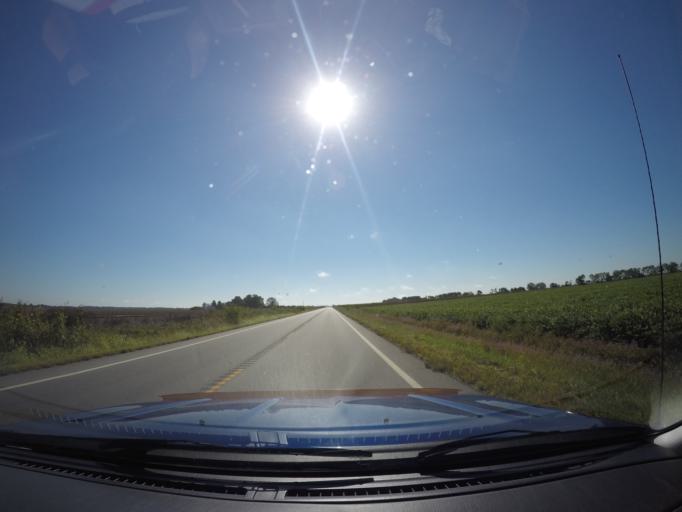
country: US
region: Kansas
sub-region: Shawnee County
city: Rossville
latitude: 39.1590
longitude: -95.9953
